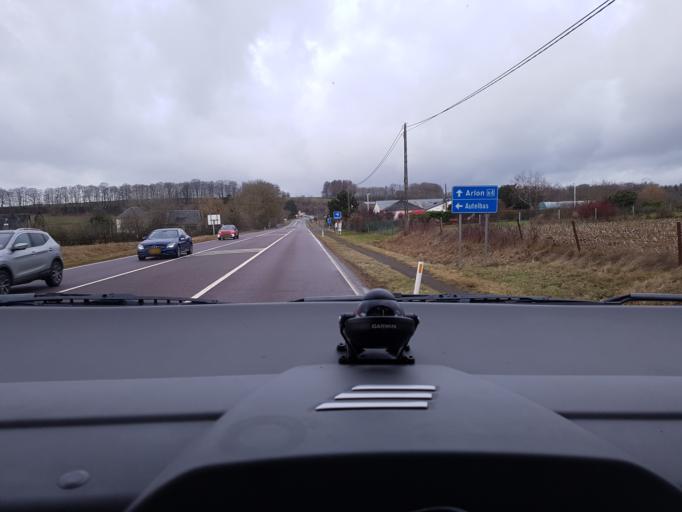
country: LU
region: Luxembourg
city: Eischen
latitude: 49.6579
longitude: 5.8638
